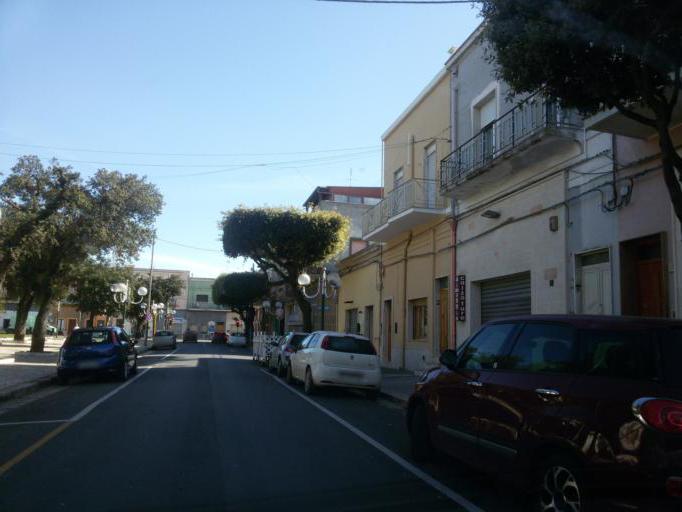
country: IT
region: Apulia
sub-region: Provincia di Brindisi
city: Mesagne
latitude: 40.5612
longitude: 17.8053
